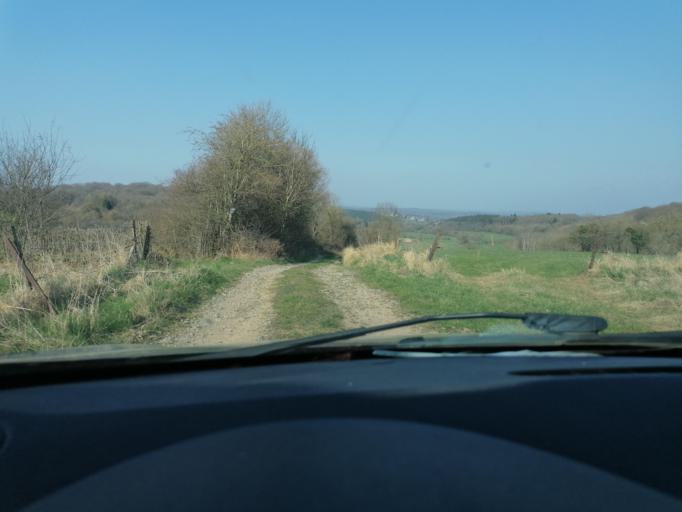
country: BE
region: Wallonia
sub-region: Province du Hainaut
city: Chimay
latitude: 50.0478
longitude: 4.3862
